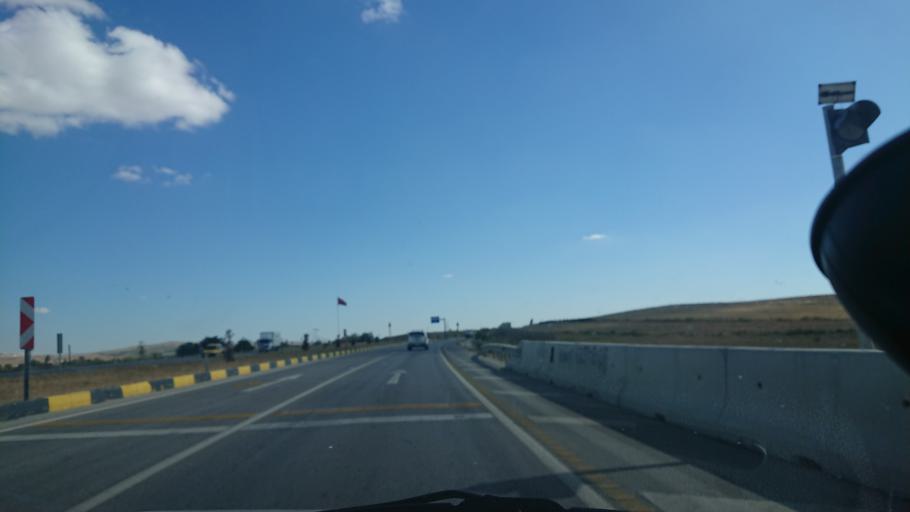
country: TR
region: Eskisehir
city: Mahmudiye
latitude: 39.5198
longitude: 30.9608
